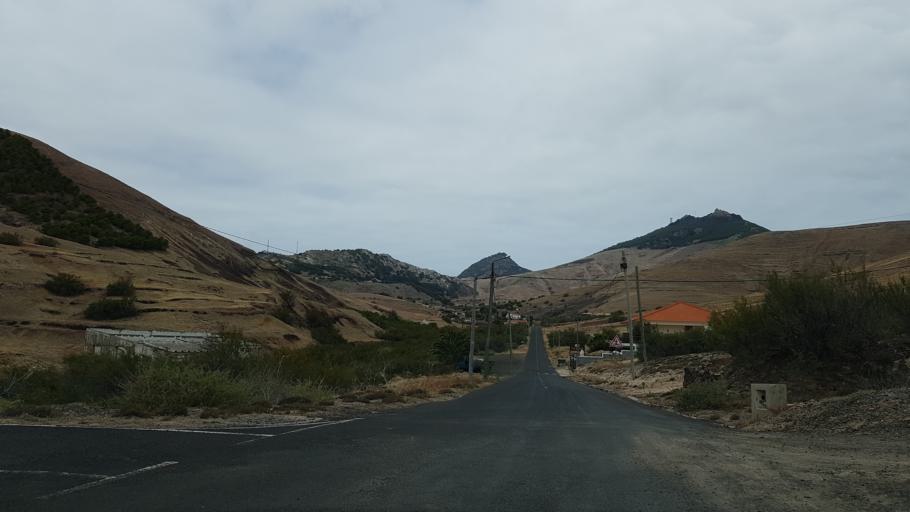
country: PT
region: Madeira
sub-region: Porto Santo
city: Vila de Porto Santo
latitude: 33.0699
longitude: -16.2986
